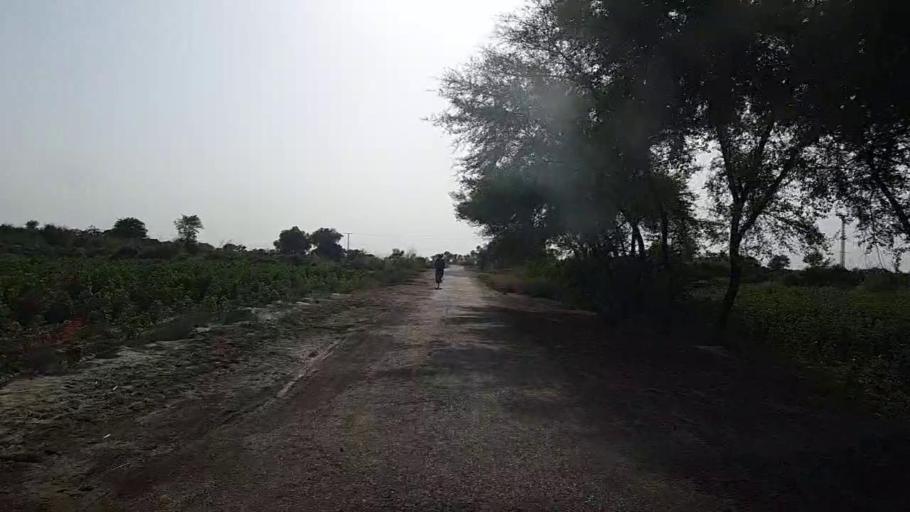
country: PK
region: Sindh
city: Pad Idan
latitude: 26.8532
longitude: 68.3171
